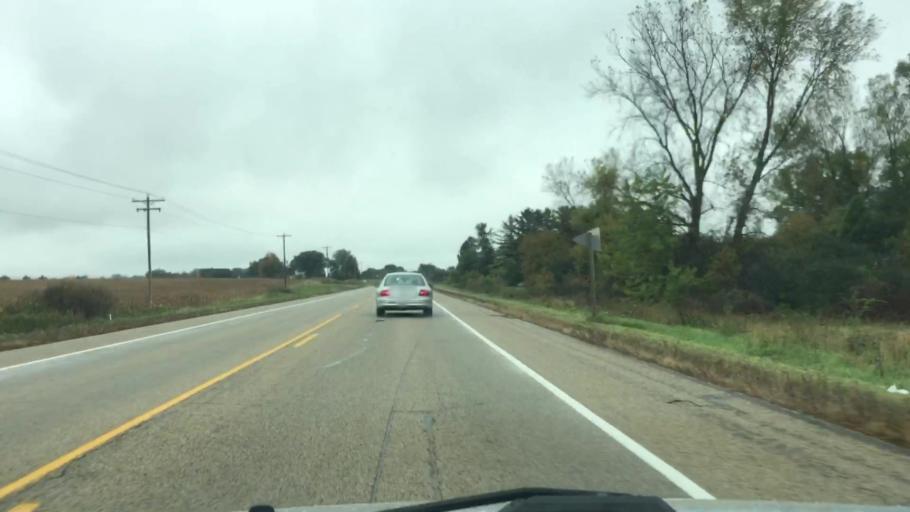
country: US
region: Wisconsin
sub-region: Jefferson County
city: Palmyra
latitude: 42.8685
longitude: -88.6464
